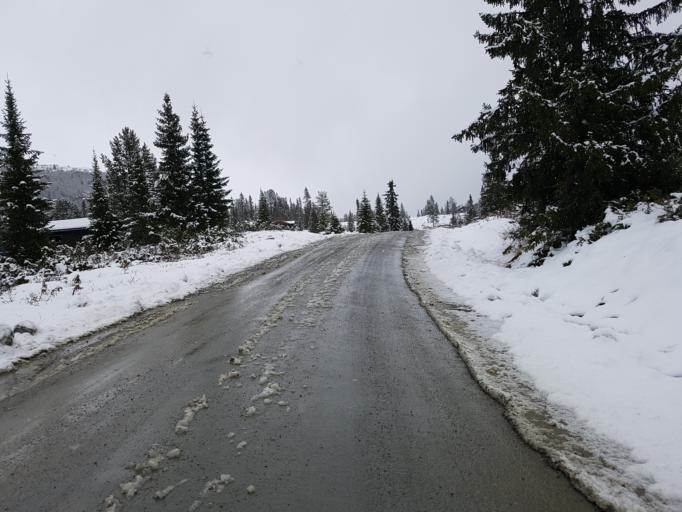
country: NO
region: Oppland
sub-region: Sel
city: Otta
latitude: 61.8067
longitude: 9.6871
